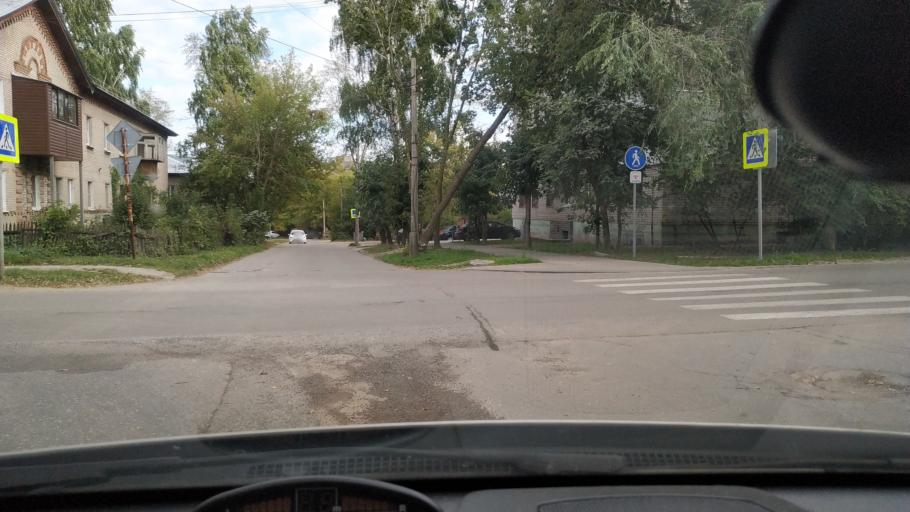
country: RU
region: Rjazan
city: Ryazan'
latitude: 54.6038
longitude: 39.7222
